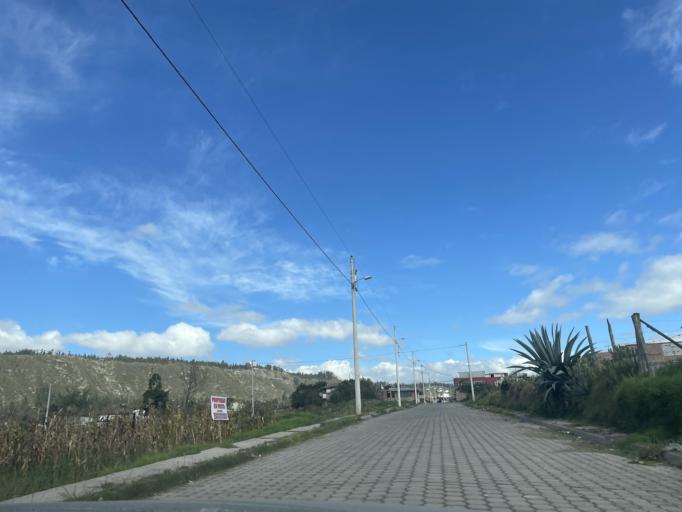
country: EC
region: Chimborazo
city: Guano
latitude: -1.6063
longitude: -78.6289
